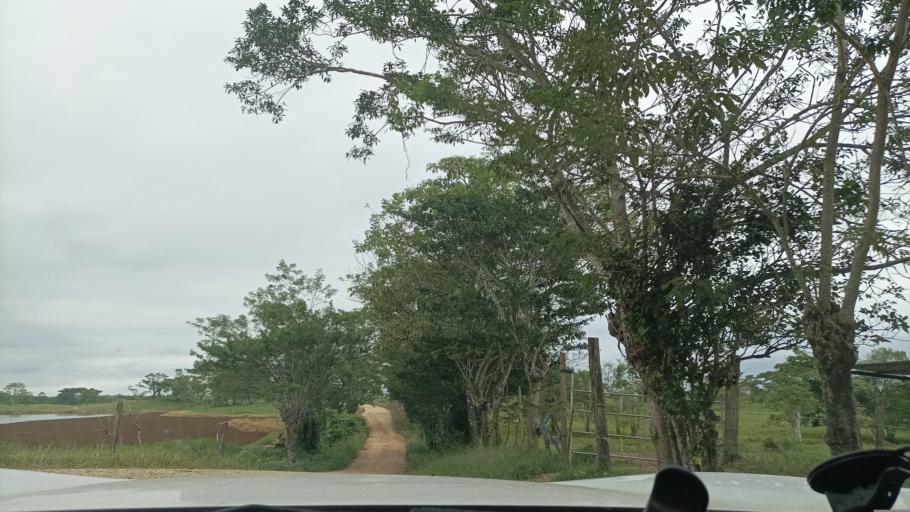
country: MX
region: Veracruz
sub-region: Texistepec
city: Venustiano Carranza (Pena Blanca)
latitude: 17.5085
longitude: -94.5621
